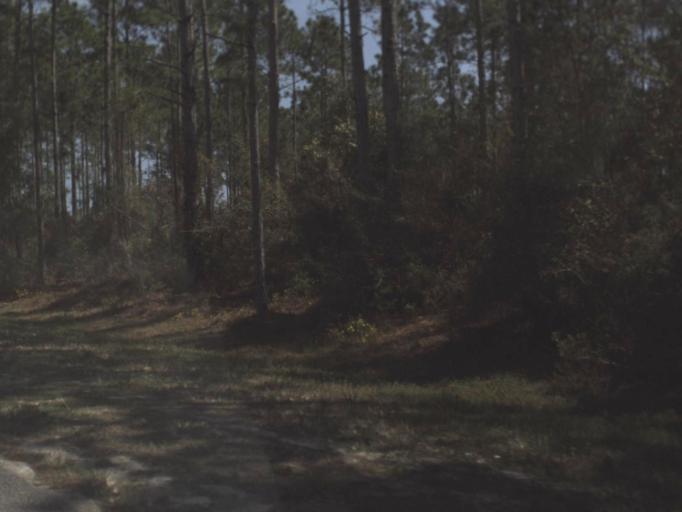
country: US
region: Florida
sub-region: Gulf County
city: Port Saint Joe
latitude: 29.7765
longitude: -85.2752
